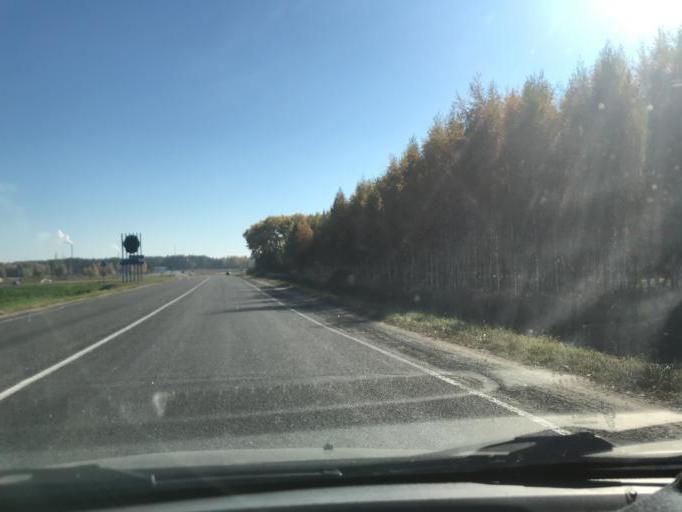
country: BY
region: Gomel
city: Kastsyukowka
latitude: 52.4544
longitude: 30.8215
